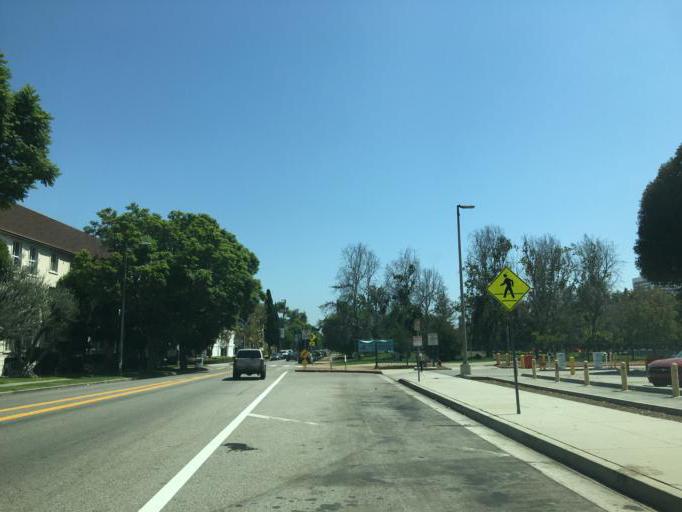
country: US
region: California
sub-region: Los Angeles County
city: Westwood, Los Angeles
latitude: 34.0559
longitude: -118.4462
